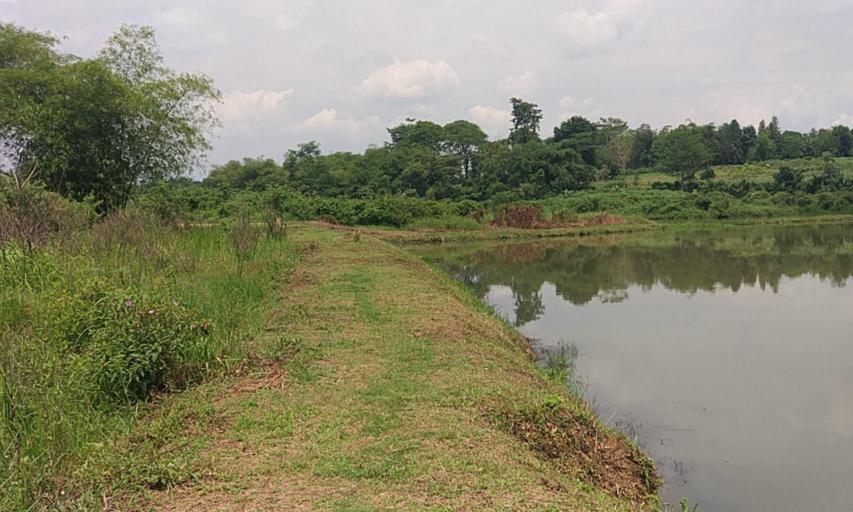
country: ID
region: West Java
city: Parung
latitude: -6.4754
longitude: 106.7757
